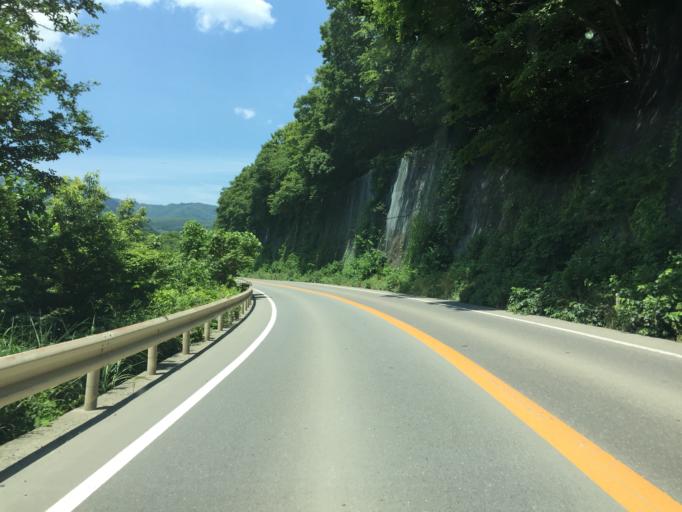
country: JP
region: Miyagi
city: Marumori
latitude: 37.7658
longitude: 140.8554
